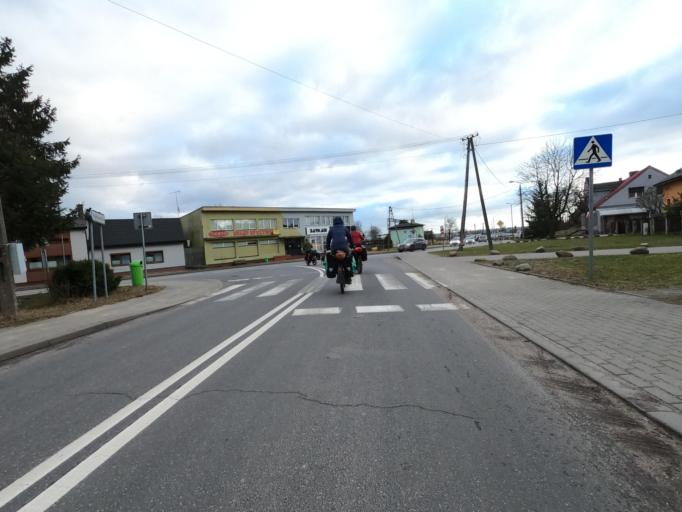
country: PL
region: Greater Poland Voivodeship
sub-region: Powiat pilski
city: Bialosliwie
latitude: 53.0975
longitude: 17.1191
